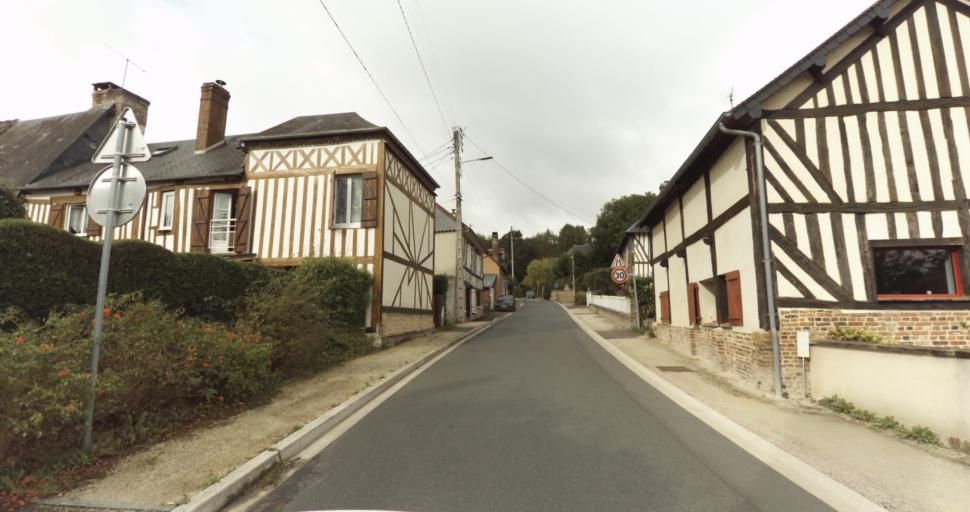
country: FR
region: Lower Normandy
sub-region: Departement de l'Orne
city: Vimoutiers
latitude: 48.9263
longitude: 0.1903
